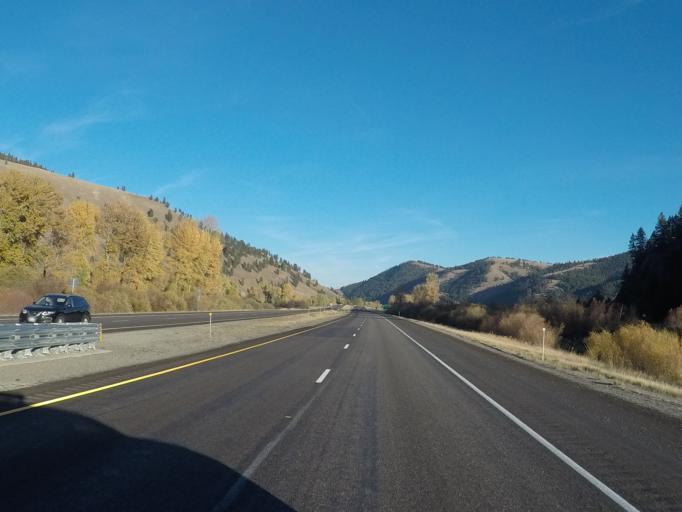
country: US
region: Montana
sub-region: Missoula County
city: Clinton
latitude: 46.7000
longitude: -113.4442
